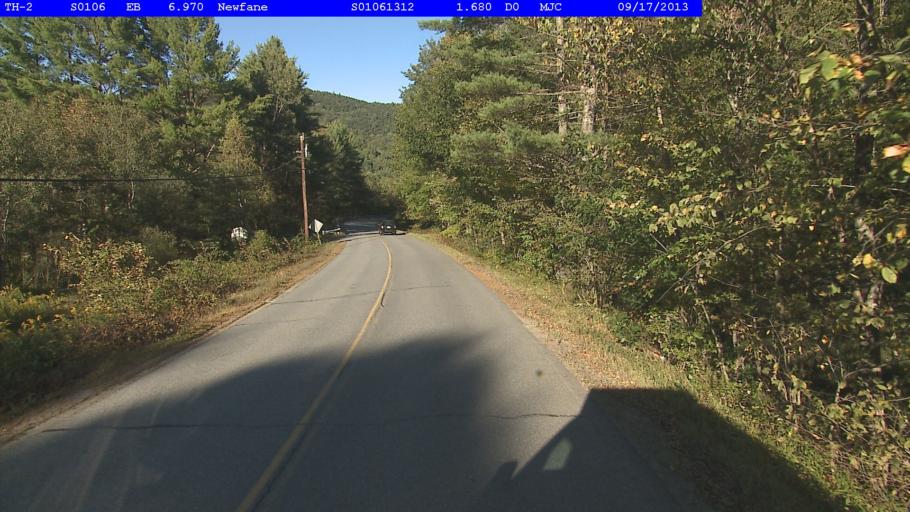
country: US
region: Vermont
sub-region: Windham County
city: Dover
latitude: 42.9447
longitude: -72.7370
